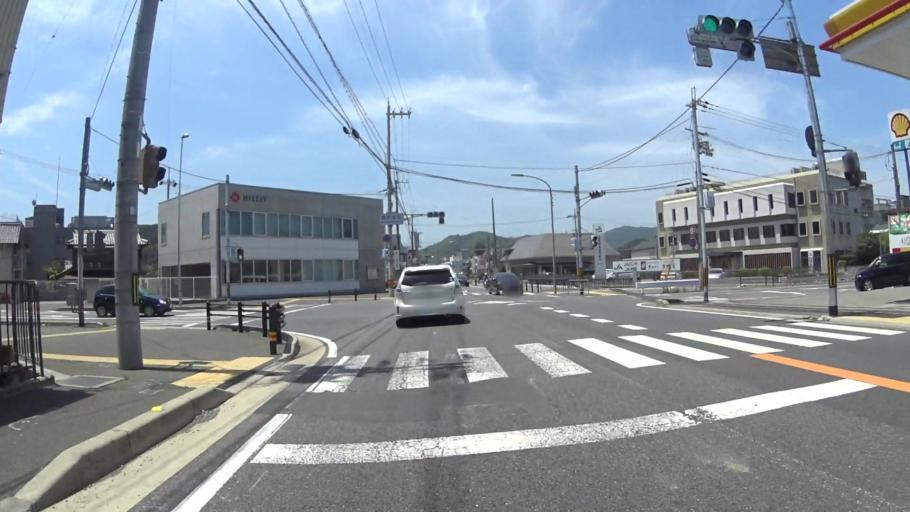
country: JP
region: Kyoto
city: Kameoka
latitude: 35.1093
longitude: 135.4750
